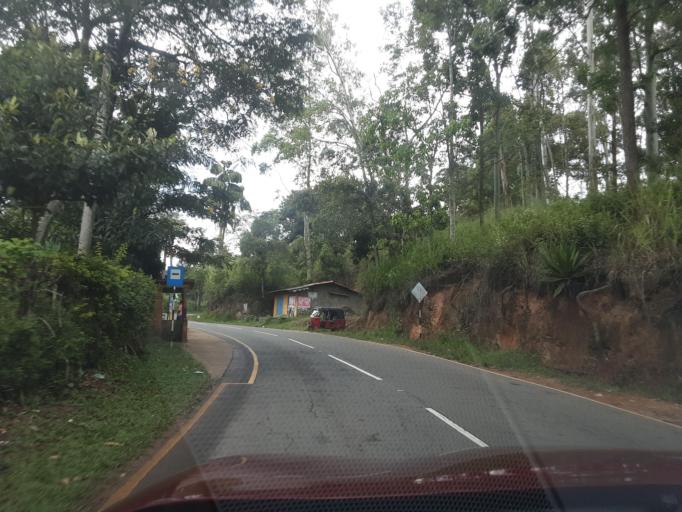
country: LK
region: Uva
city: Haputale
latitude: 6.8586
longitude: 80.9668
